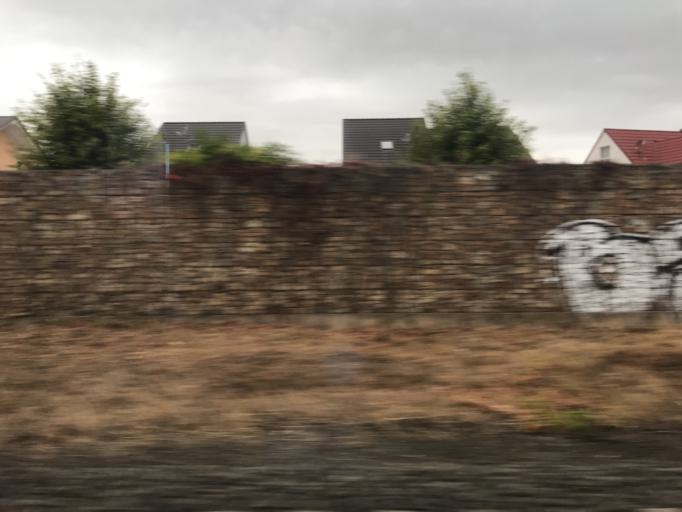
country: DE
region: Hesse
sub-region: Regierungsbezirk Darmstadt
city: Stockstadt am Rhein
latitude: 49.8112
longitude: 8.4734
